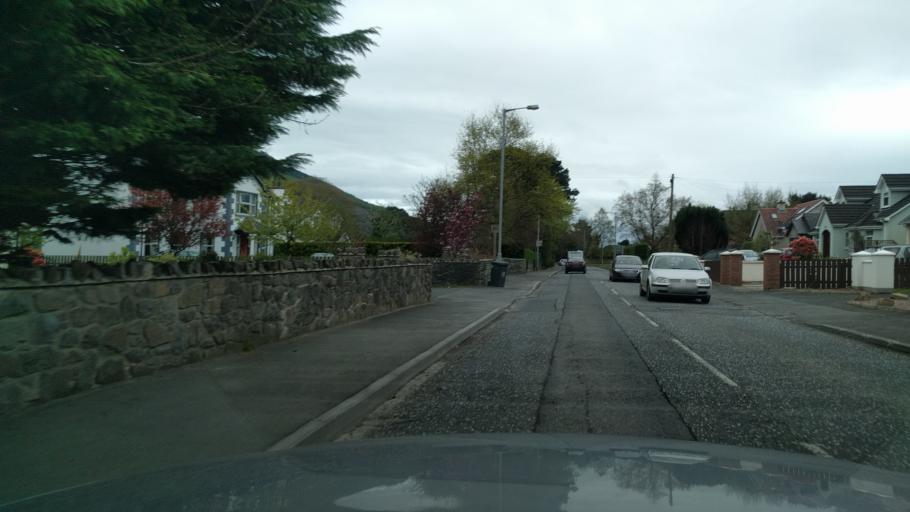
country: GB
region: Northern Ireland
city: Rostrevor
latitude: 54.0999
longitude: -6.2002
